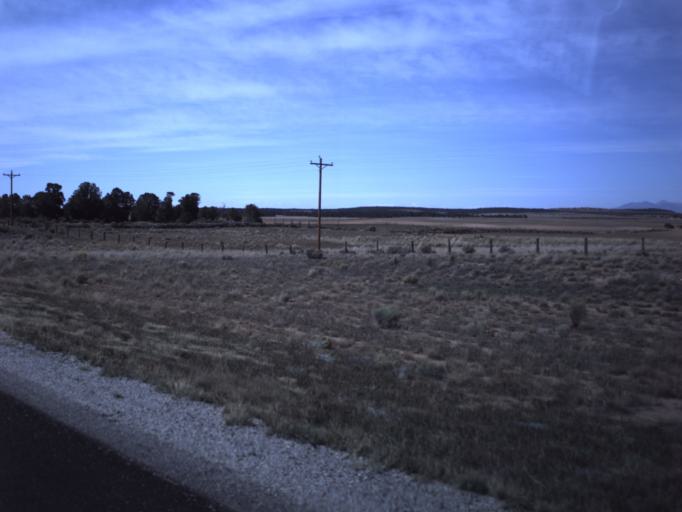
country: US
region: Colorado
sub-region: Dolores County
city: Dove Creek
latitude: 37.8273
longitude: -109.0797
